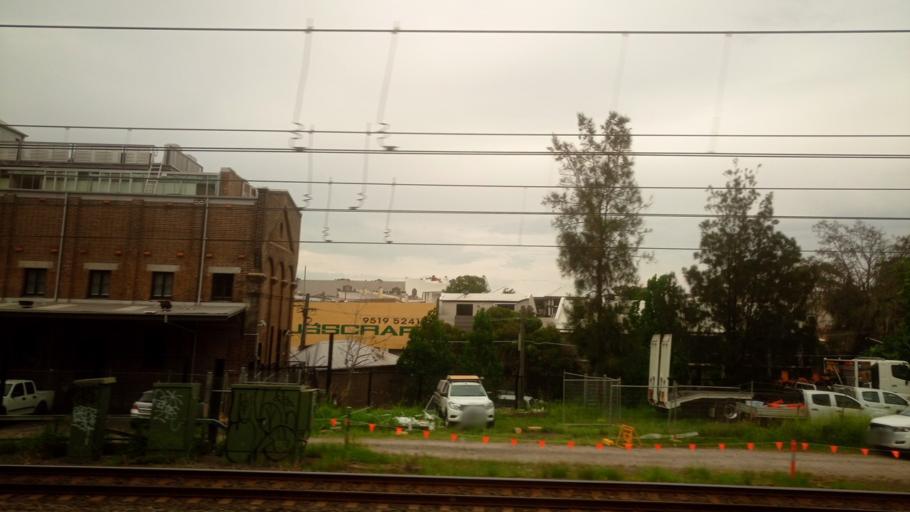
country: AU
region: New South Wales
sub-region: Marrickville
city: Newtown
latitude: -33.8970
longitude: 151.1748
